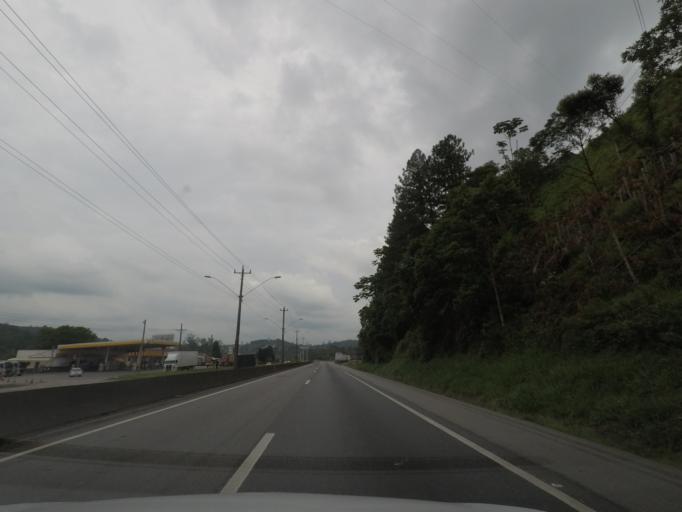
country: BR
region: Sao Paulo
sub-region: Sao Lourenco Da Serra
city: Sao Lourenco da Serra
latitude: -23.8894
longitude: -46.9808
